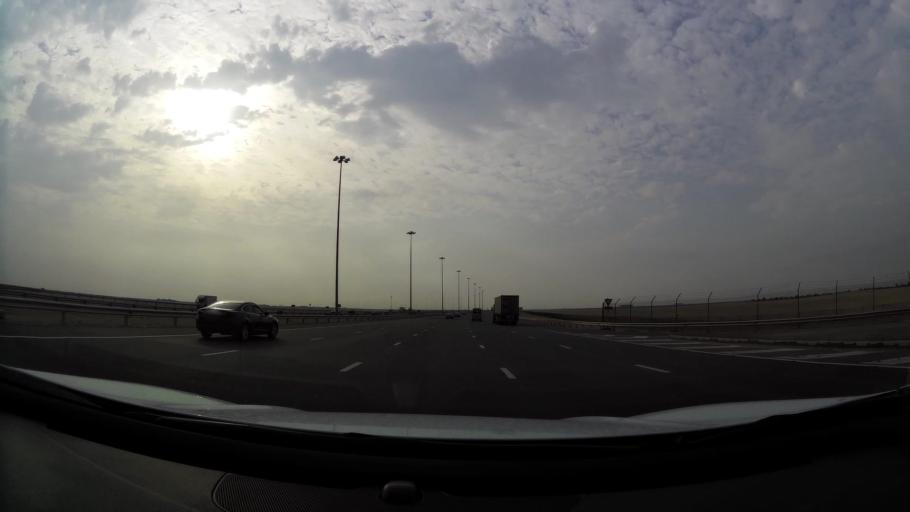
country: AE
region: Abu Dhabi
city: Abu Dhabi
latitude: 24.5404
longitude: 54.4832
